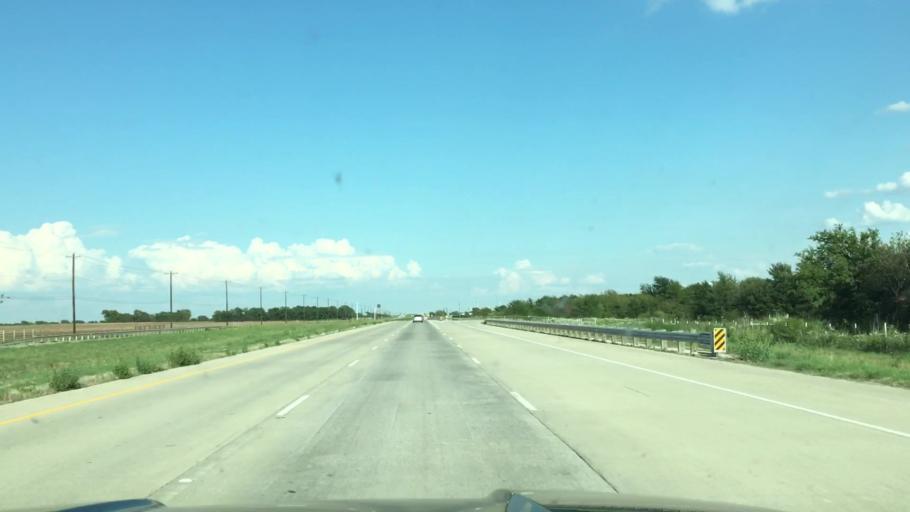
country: US
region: Texas
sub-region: Tarrant County
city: Haslet
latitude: 33.0353
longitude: -97.3613
